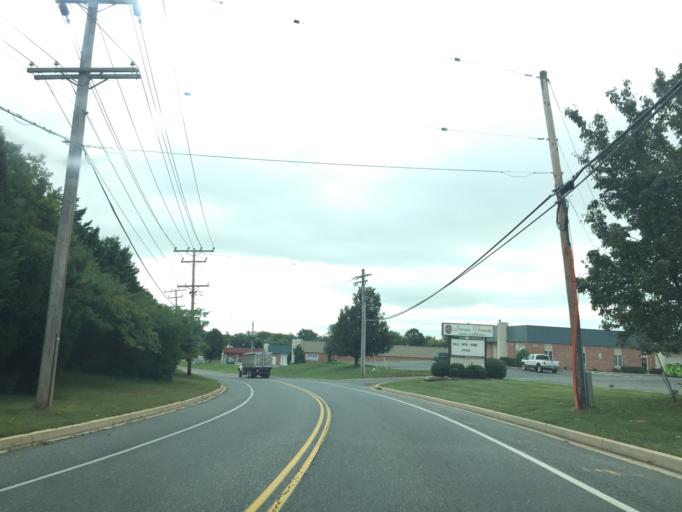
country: US
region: Maryland
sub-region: Harford County
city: Bel Air North
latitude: 39.5794
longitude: -76.3710
